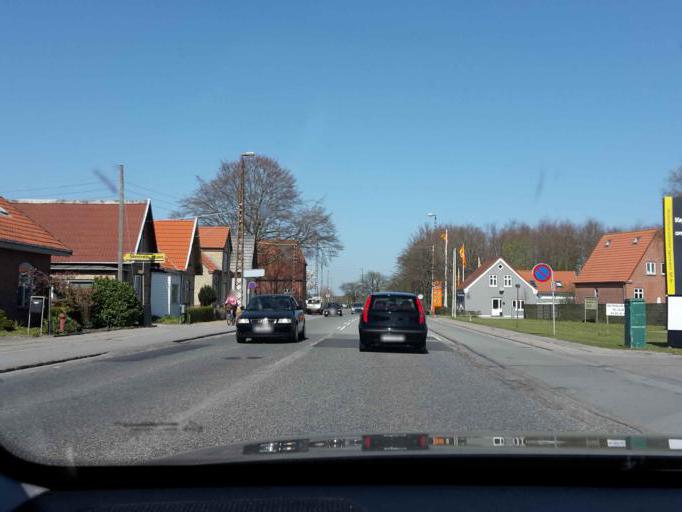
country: DK
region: South Denmark
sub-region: Odense Kommune
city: Odense
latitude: 55.3710
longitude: 10.3946
